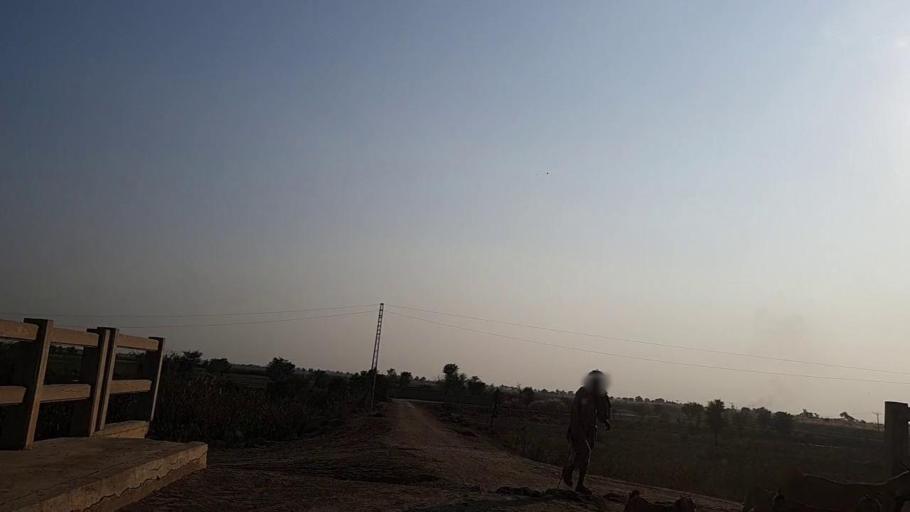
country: PK
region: Sindh
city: Sakrand
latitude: 26.0936
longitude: 68.3954
